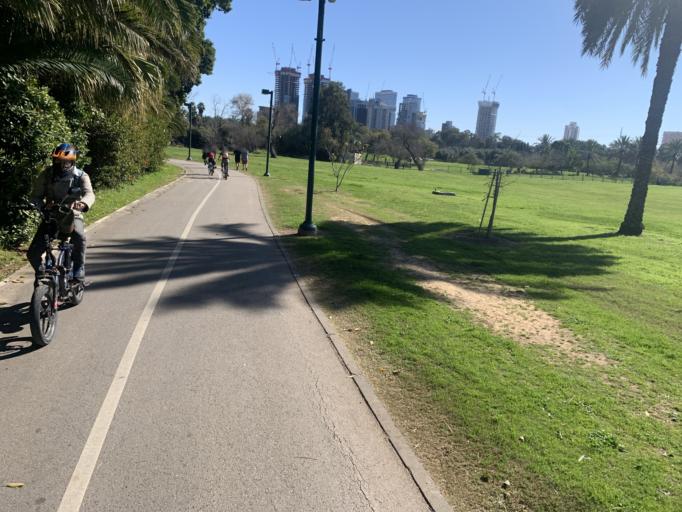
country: IL
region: Tel Aviv
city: Ramat Gan
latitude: 32.1007
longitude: 34.8118
